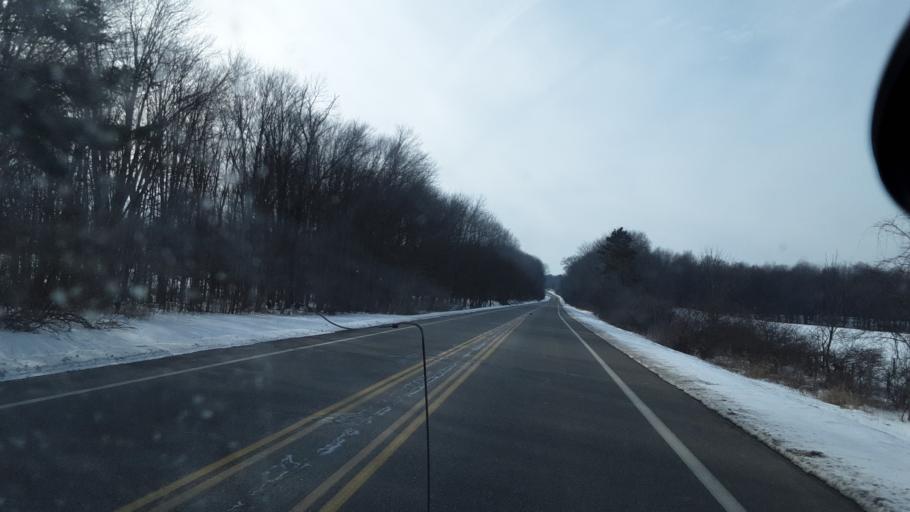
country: US
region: Ohio
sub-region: Stark County
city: Hartville
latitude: 41.0268
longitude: -81.3322
